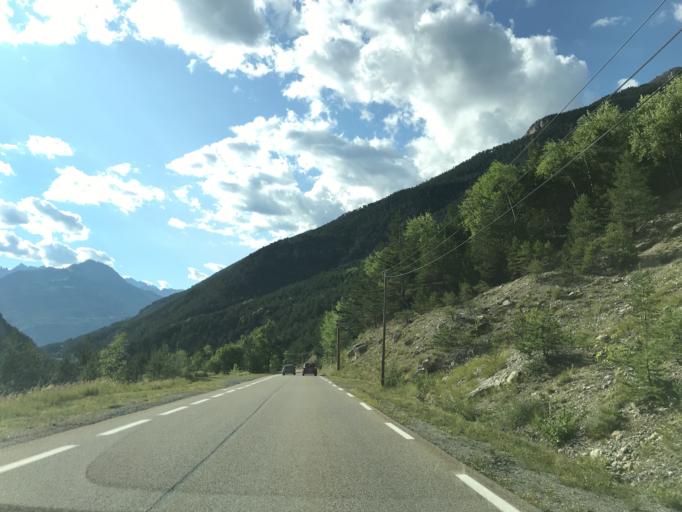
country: FR
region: Provence-Alpes-Cote d'Azur
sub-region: Departement des Hautes-Alpes
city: Briancon
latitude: 44.8750
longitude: 6.6920
